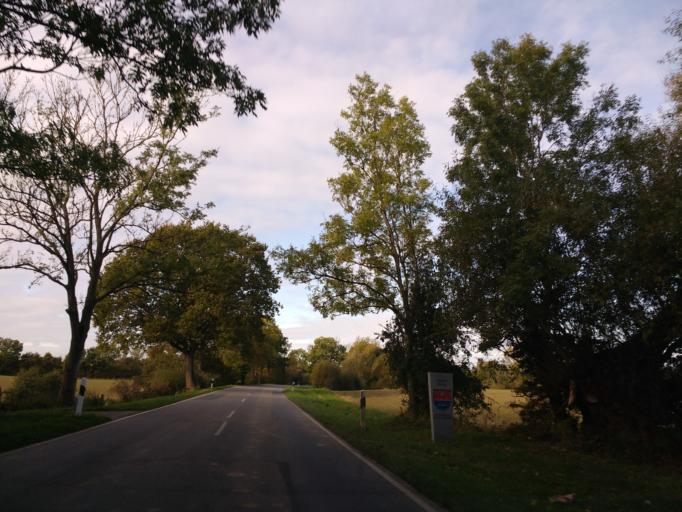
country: DE
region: Schleswig-Holstein
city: Wangels
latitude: 54.2596
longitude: 10.7158
